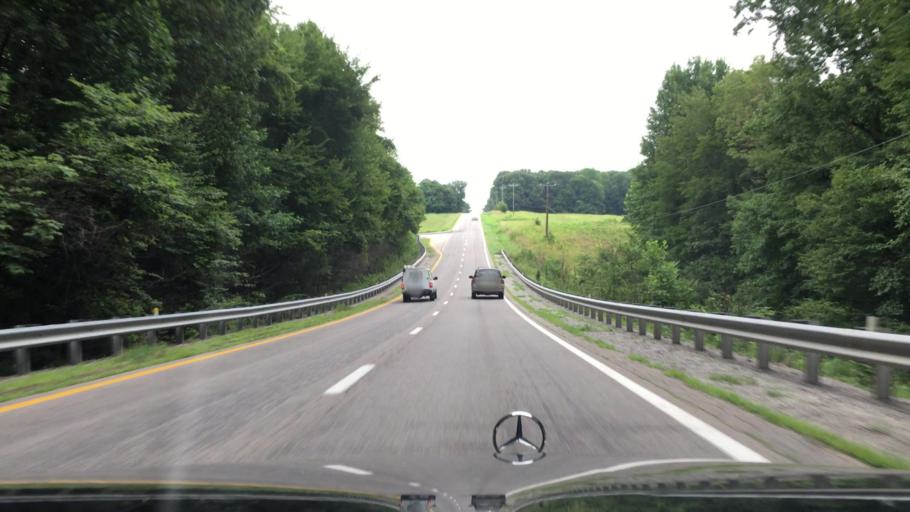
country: US
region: Virginia
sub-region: Prince Edward County
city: Hampden Sydney
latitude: 37.3062
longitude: -78.5179
